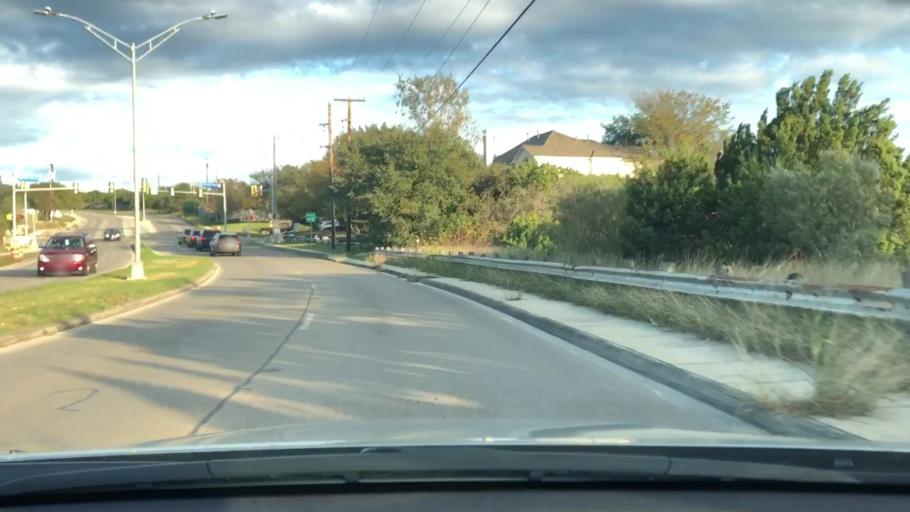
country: US
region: Texas
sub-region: Bexar County
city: Hollywood Park
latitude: 29.6343
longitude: -98.5157
